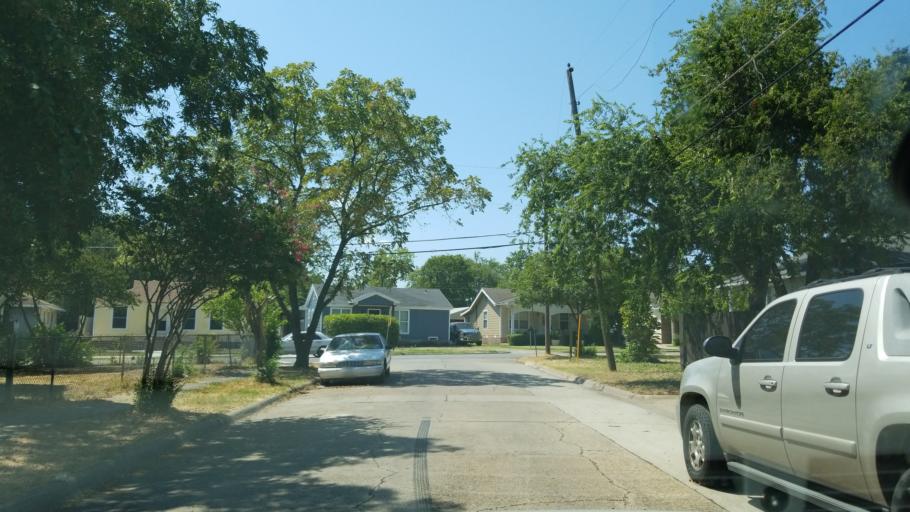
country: US
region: Texas
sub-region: Dallas County
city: Cockrell Hill
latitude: 32.7454
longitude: -96.8852
